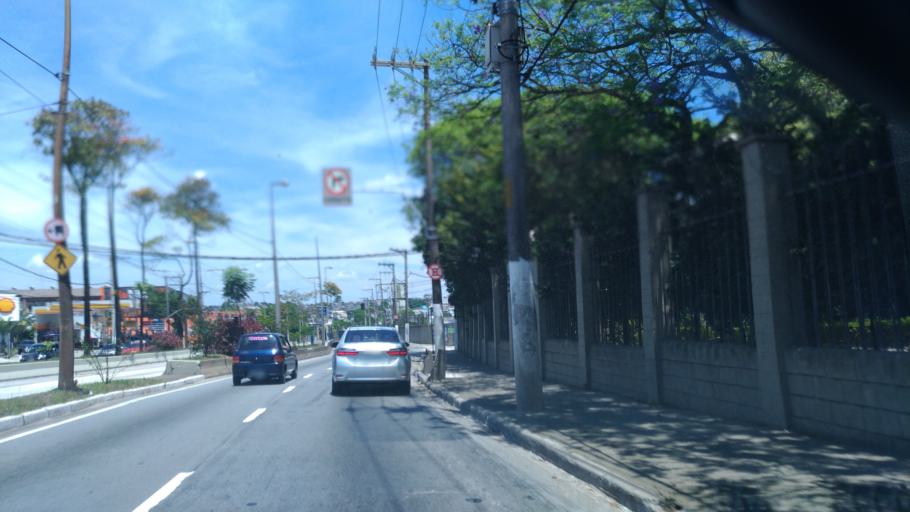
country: BR
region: Sao Paulo
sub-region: Sao Bernardo Do Campo
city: Sao Bernardo do Campo
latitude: -23.6900
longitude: -46.5760
